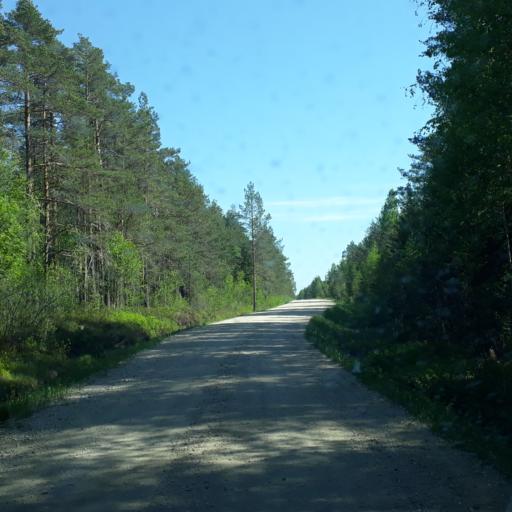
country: EE
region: Paernumaa
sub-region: Vaendra vald (alev)
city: Vandra
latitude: 58.7457
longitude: 24.9784
